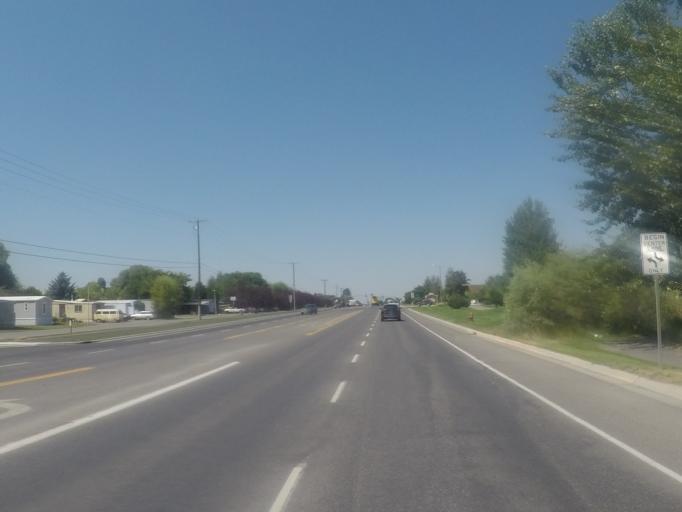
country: US
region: Montana
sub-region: Gallatin County
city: Bozeman
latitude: 45.6931
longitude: -111.0578
